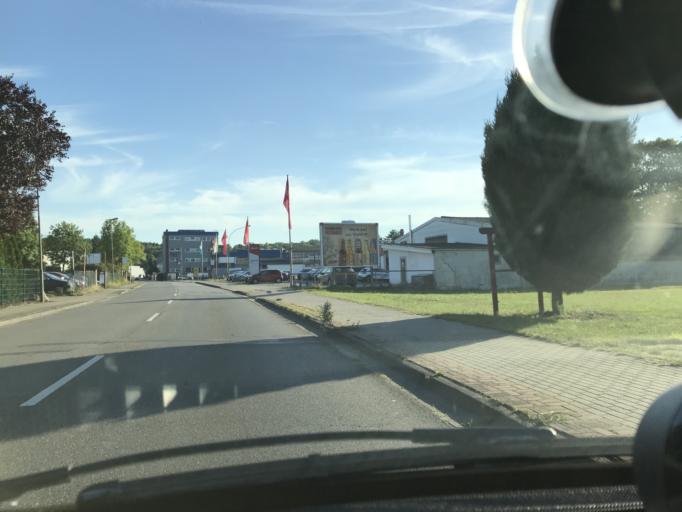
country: DE
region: Lower Saxony
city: Buxtehude
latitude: 53.4653
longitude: 9.7194
